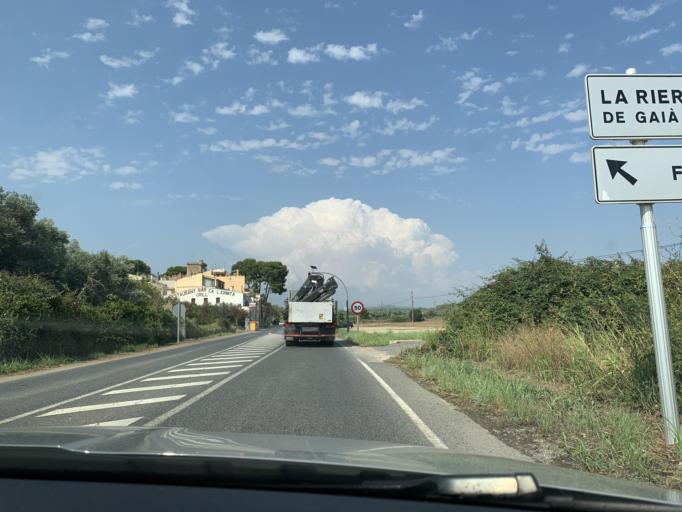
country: ES
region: Catalonia
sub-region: Provincia de Tarragona
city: Altafulla
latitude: 41.1439
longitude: 1.3586
